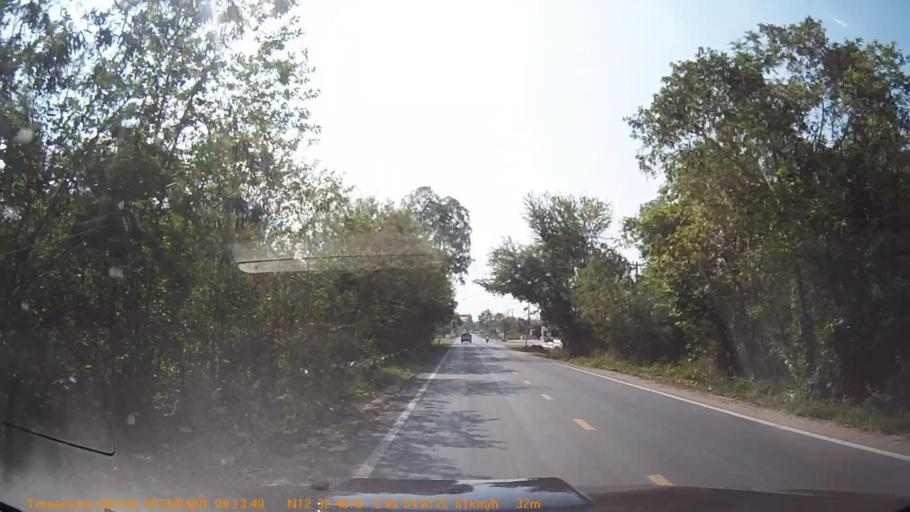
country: TH
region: Prachuap Khiri Khan
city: Hua Hin
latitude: 12.5410
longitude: 99.9003
